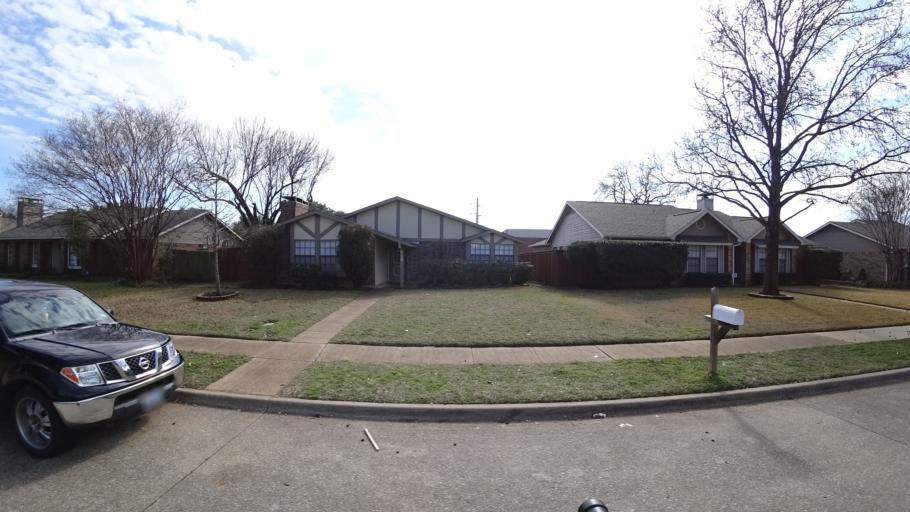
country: US
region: Texas
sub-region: Denton County
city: Lewisville
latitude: 33.0213
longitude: -97.0086
